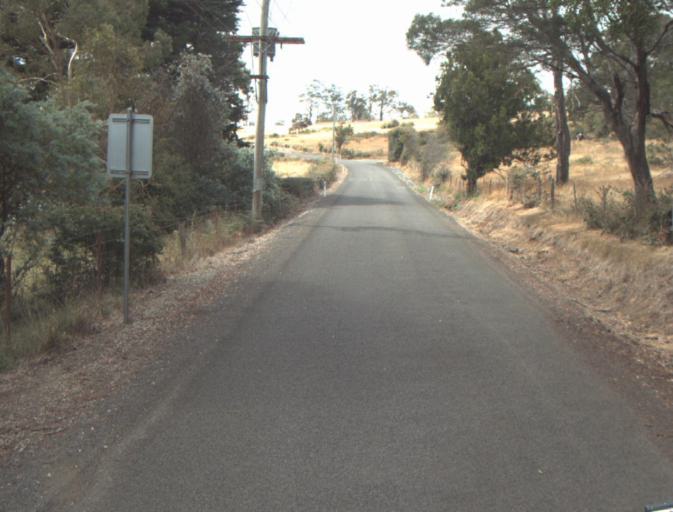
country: AU
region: Tasmania
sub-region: Launceston
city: Mayfield
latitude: -41.3147
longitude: 146.9969
